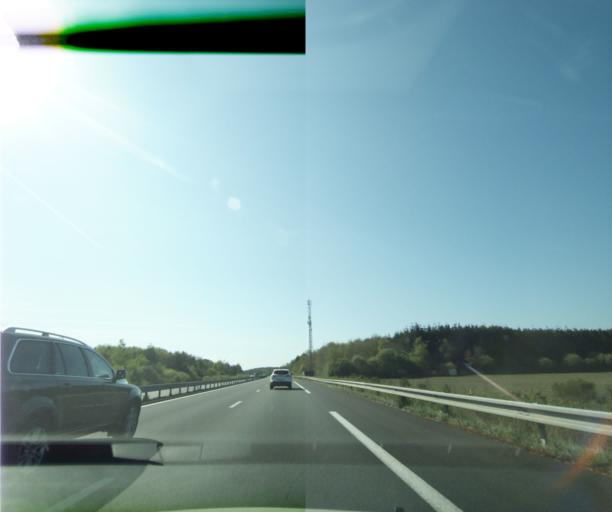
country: FR
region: Centre
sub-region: Departement du Loiret
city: Jouy-le-Potier
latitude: 47.7637
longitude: 1.8529
